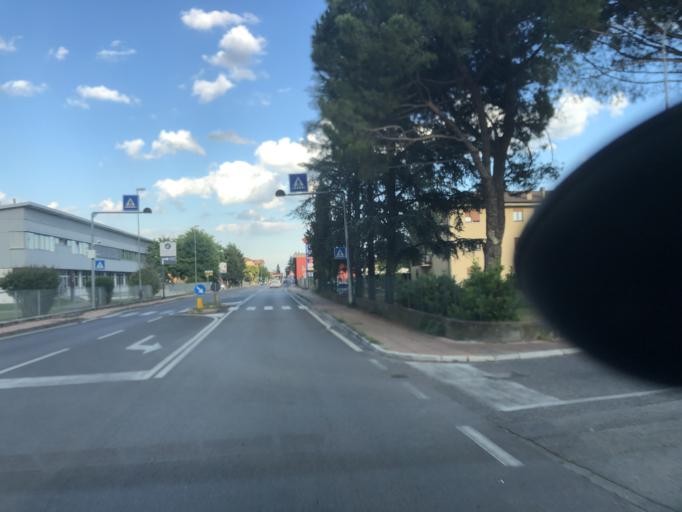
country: IT
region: Veneto
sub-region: Provincia di Verona
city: Pescantina
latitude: 45.4967
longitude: 10.8705
